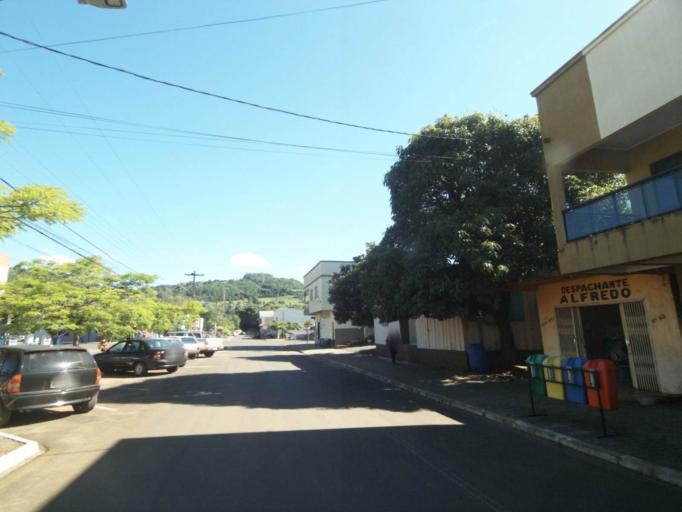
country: BR
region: Parana
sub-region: Ampere
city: Ampere
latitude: -26.1726
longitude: -53.3620
